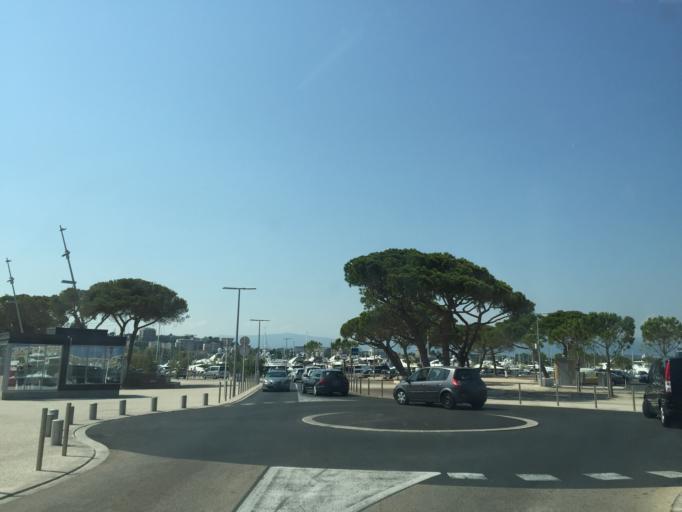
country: FR
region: Provence-Alpes-Cote d'Azur
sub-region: Departement des Alpes-Maritimes
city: Antibes
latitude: 43.5833
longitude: 7.1277
